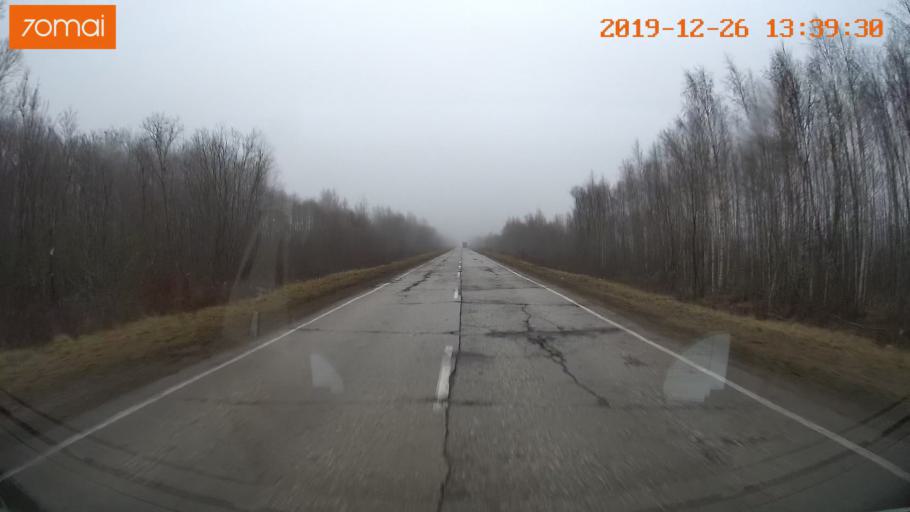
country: RU
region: Vologda
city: Sheksna
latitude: 58.7514
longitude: 38.4124
